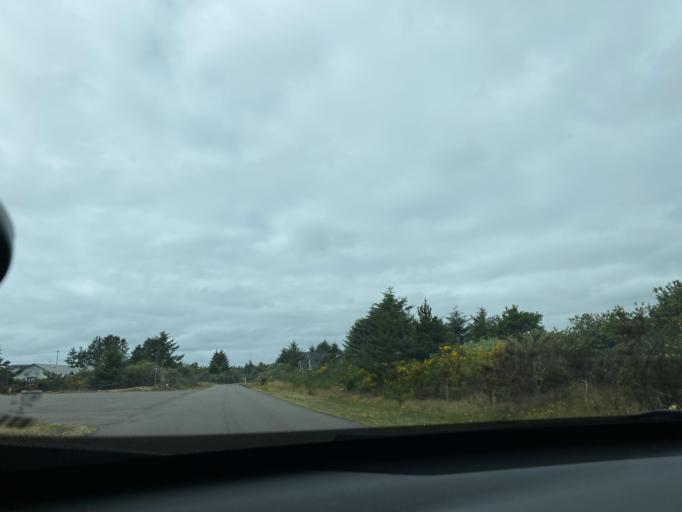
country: US
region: Washington
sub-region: Grays Harbor County
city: Ocean Shores
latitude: 46.9507
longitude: -124.1425
